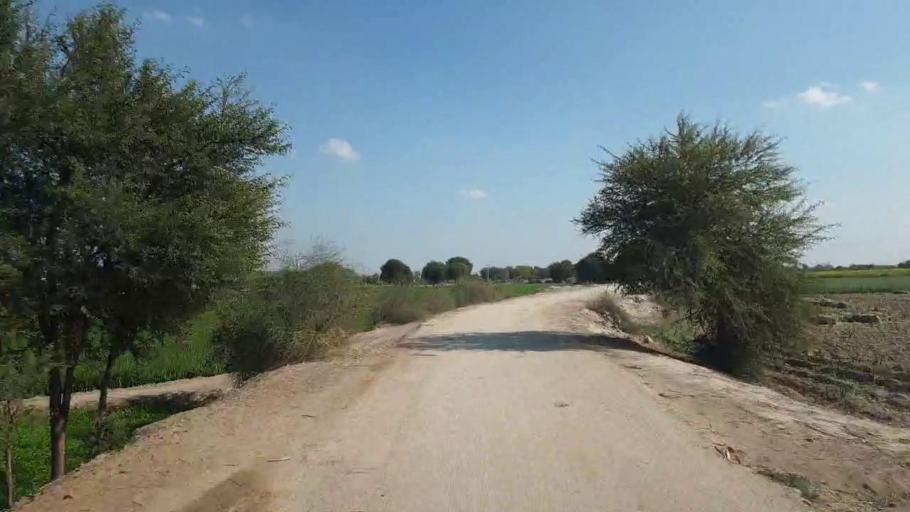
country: PK
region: Sindh
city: Shahpur Chakar
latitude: 26.0897
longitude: 68.5773
